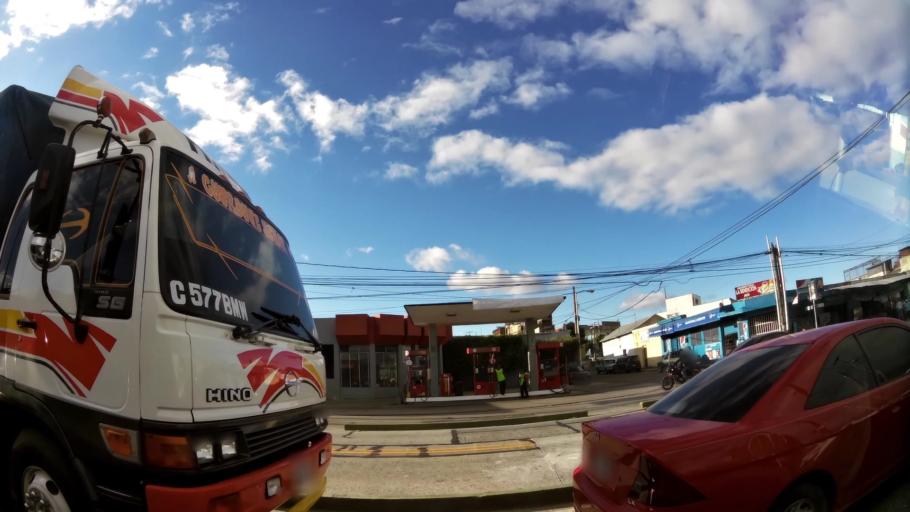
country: GT
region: Guatemala
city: Guatemala City
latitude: 14.6218
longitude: -90.5251
